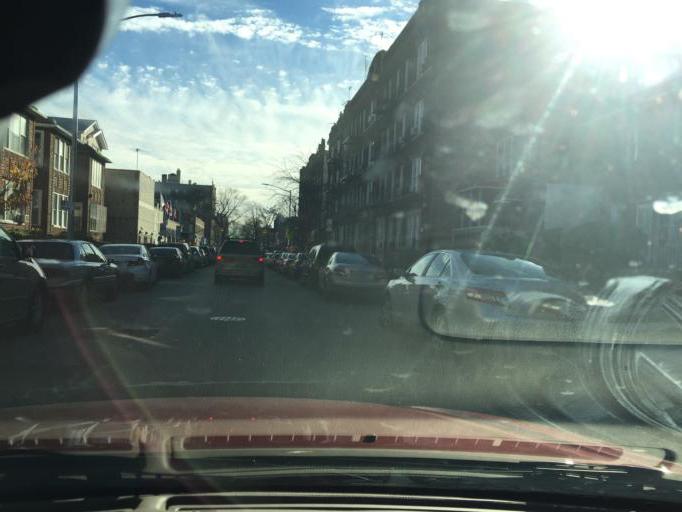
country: US
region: New York
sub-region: Kings County
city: Brooklyn
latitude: 40.6261
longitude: -73.9625
